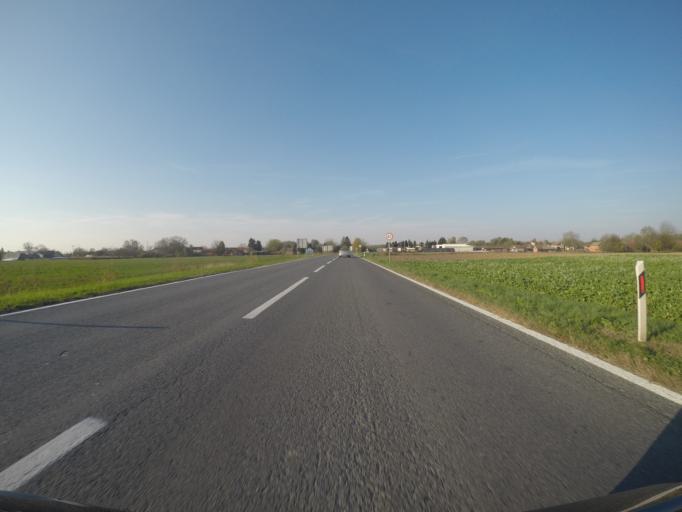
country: HU
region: Somogy
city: Barcs
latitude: 45.9383
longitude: 17.4607
